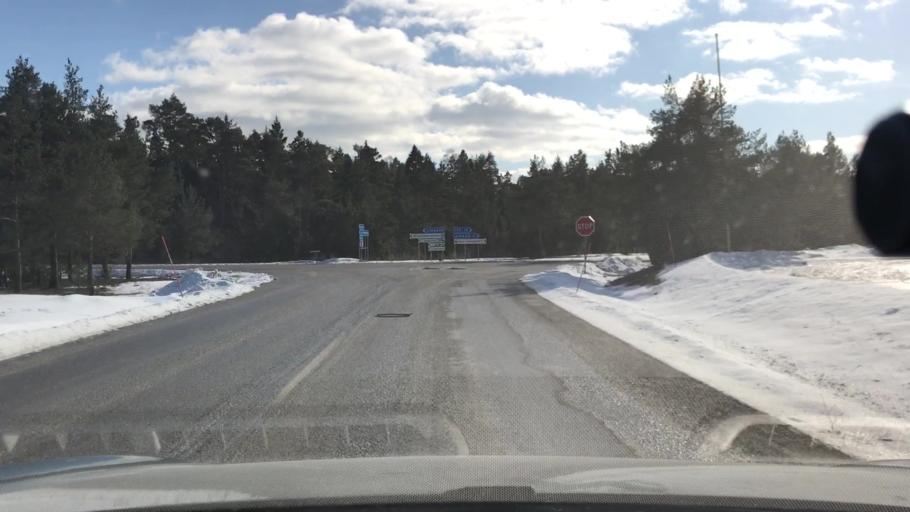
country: SE
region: Gotland
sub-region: Gotland
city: Hemse
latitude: 57.3408
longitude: 18.6924
